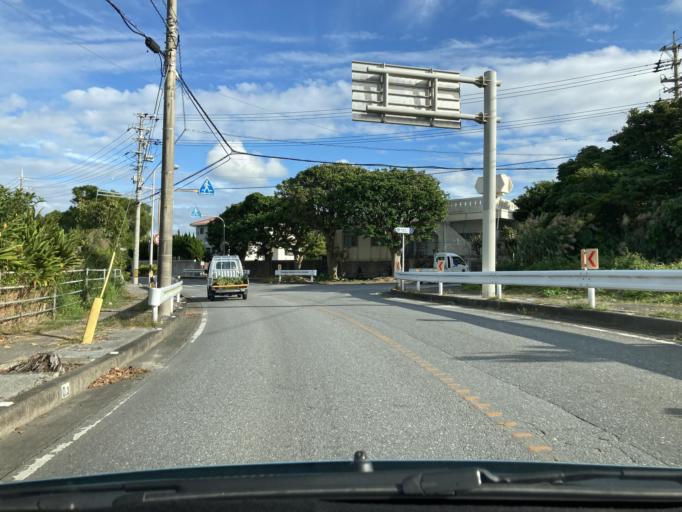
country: JP
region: Okinawa
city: Itoman
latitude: 26.1341
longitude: 127.6988
